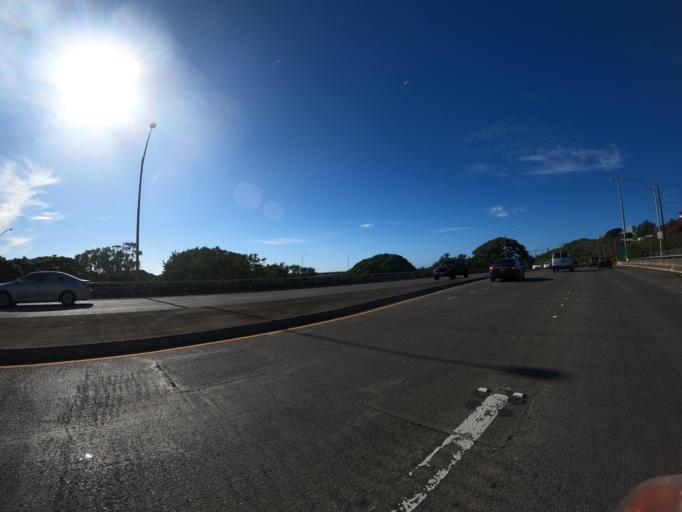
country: US
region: Hawaii
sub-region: Honolulu County
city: Halawa Heights
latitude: 21.3496
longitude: -157.8955
